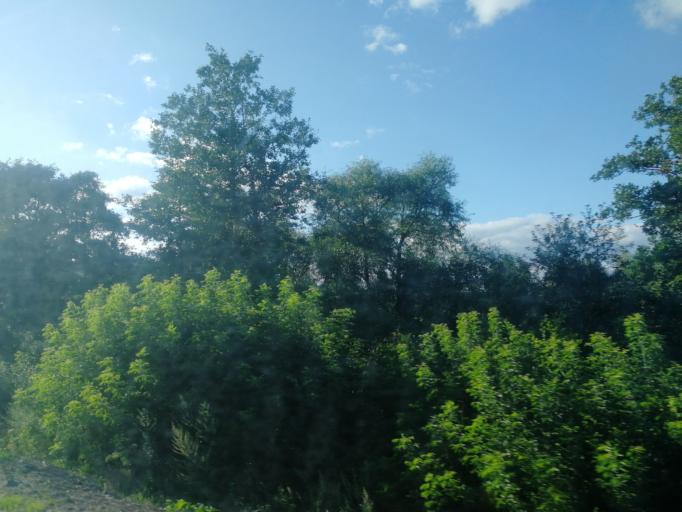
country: RU
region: Tula
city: Novogurovskiy
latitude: 54.2809
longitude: 37.1823
